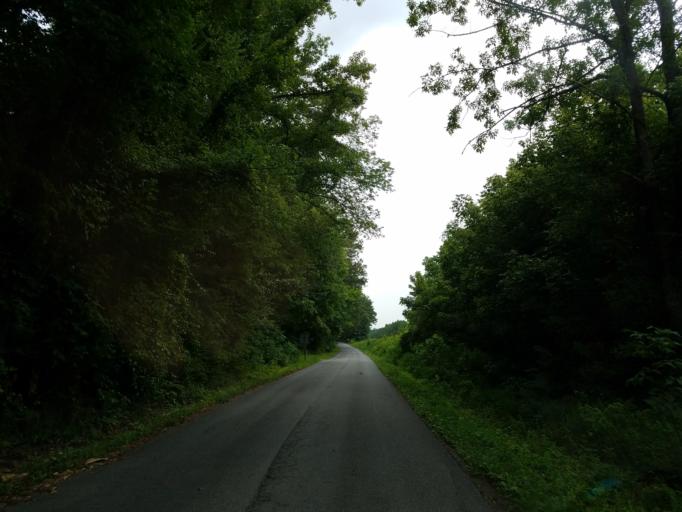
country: US
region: Georgia
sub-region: Bartow County
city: Rydal
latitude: 34.2640
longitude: -84.7611
